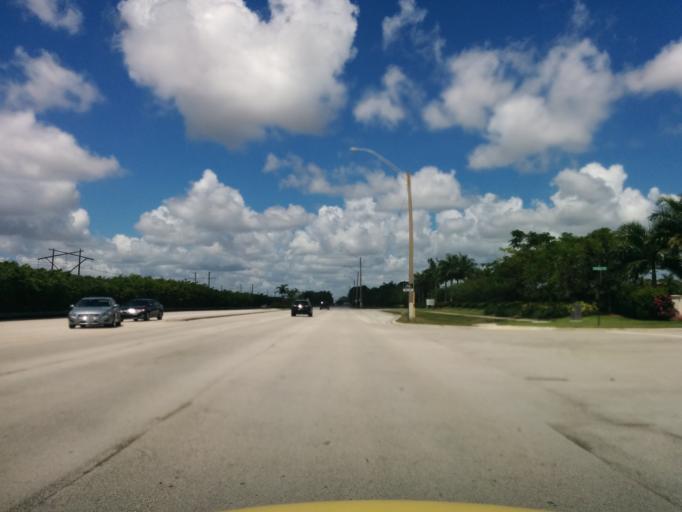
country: US
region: Florida
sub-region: Broward County
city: Cooper City
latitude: 26.0311
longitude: -80.2563
